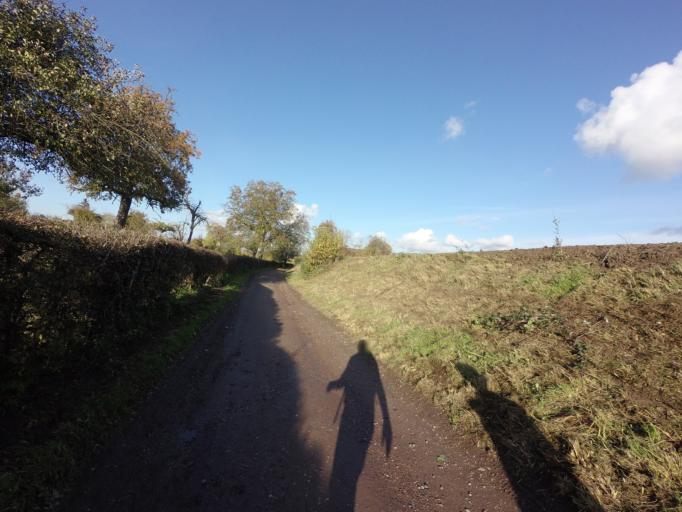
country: BE
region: Wallonia
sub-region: Province de Liege
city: Plombieres
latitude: 50.7669
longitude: 5.9184
